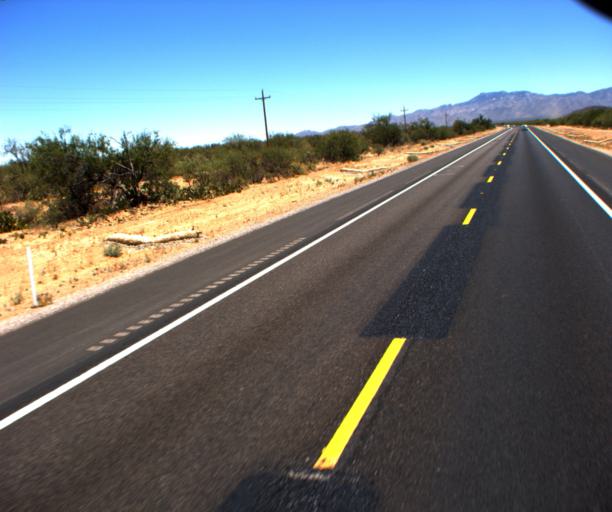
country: US
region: Arizona
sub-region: Pima County
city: Sells
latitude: 31.9191
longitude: -111.8335
